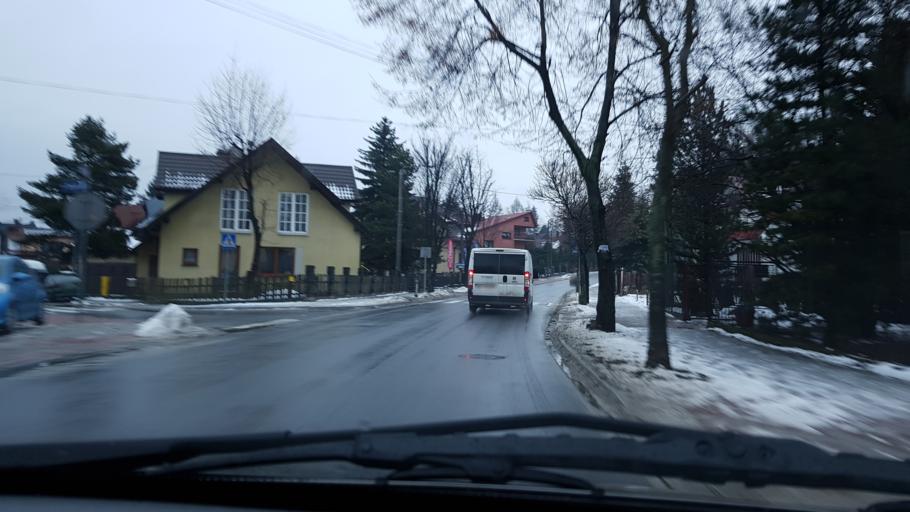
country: PL
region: Lesser Poland Voivodeship
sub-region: Powiat nowotarski
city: Nowy Targ
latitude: 49.4790
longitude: 20.0466
